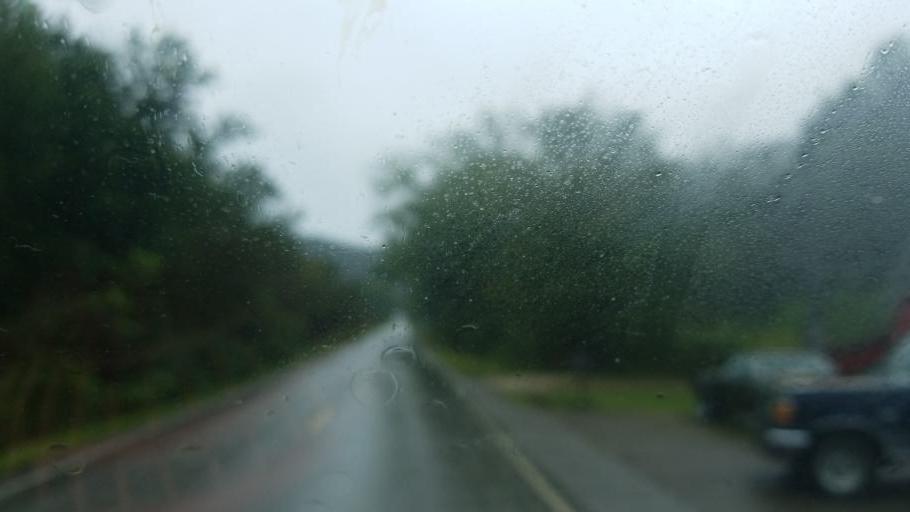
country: US
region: Kentucky
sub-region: Greenup County
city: South Shore
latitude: 38.6875
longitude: -82.9266
